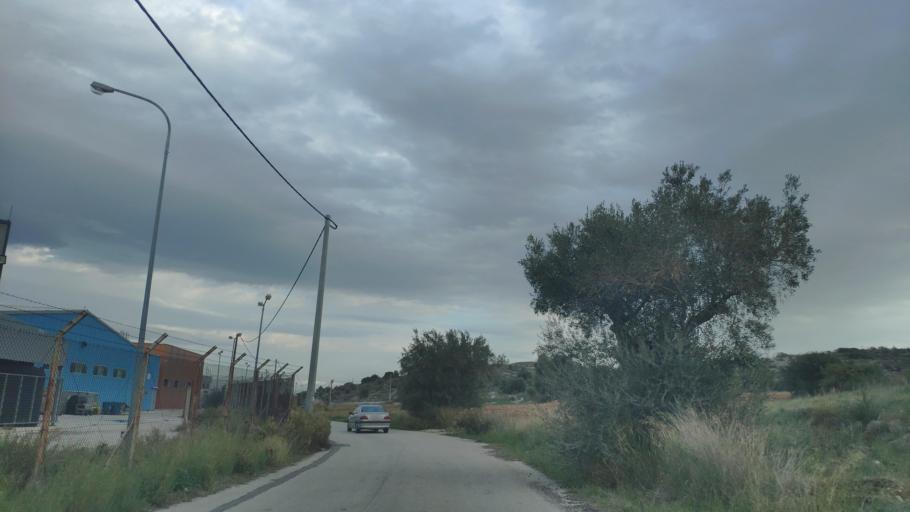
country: GR
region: Attica
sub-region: Nomarchia Dytikis Attikis
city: Megara
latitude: 37.9793
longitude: 23.3798
